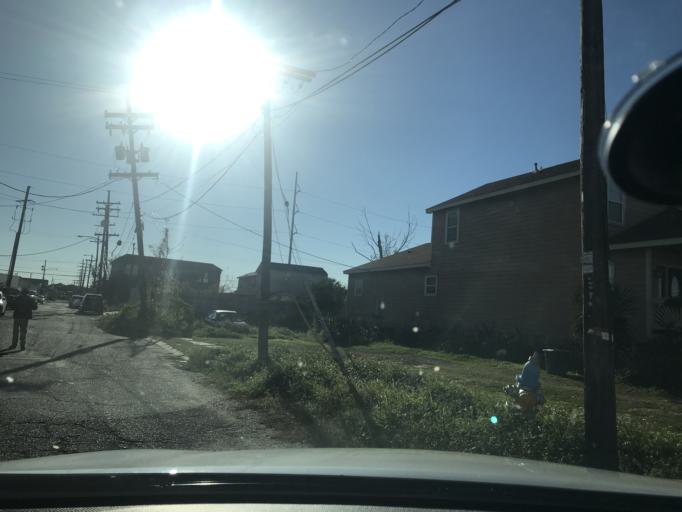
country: US
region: Louisiana
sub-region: Orleans Parish
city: New Orleans
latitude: 29.9545
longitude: -90.0989
